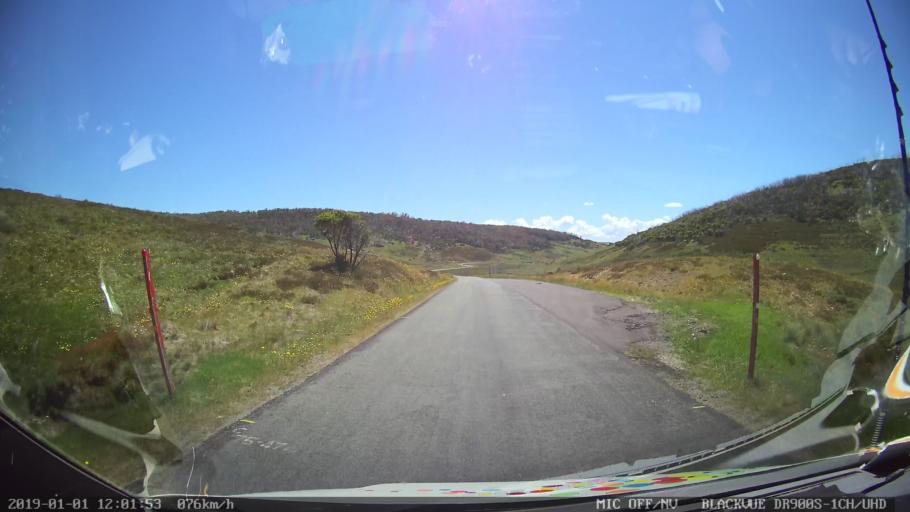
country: AU
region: New South Wales
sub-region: Snowy River
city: Jindabyne
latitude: -35.8770
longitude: 148.4727
